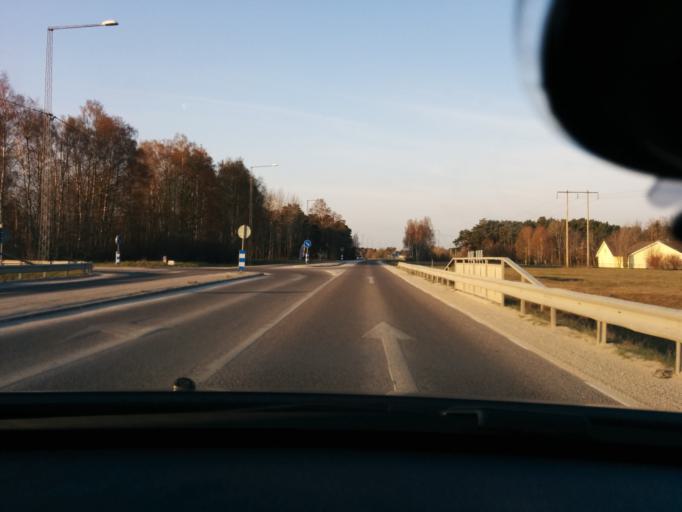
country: SE
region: Gotland
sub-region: Gotland
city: Visby
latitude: 57.6189
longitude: 18.3166
